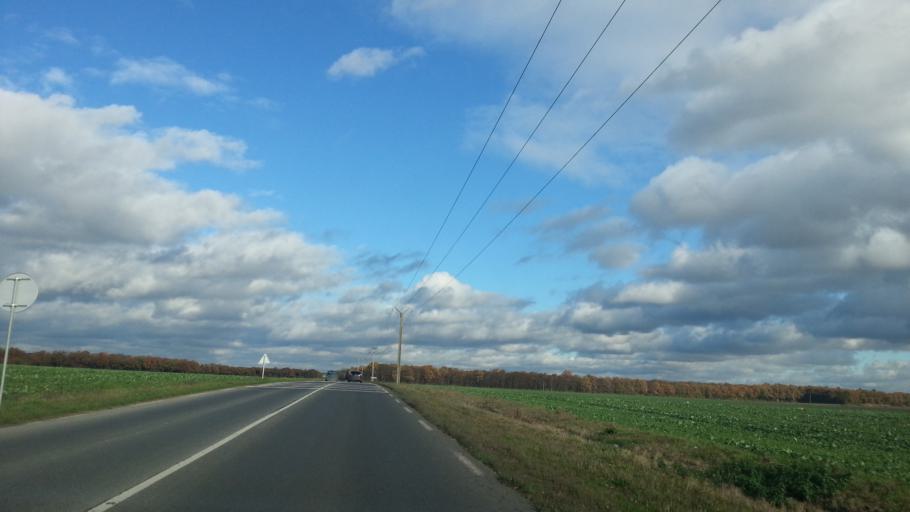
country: FR
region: Picardie
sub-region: Departement de l'Oise
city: Gouvieux
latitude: 49.2004
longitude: 2.4353
